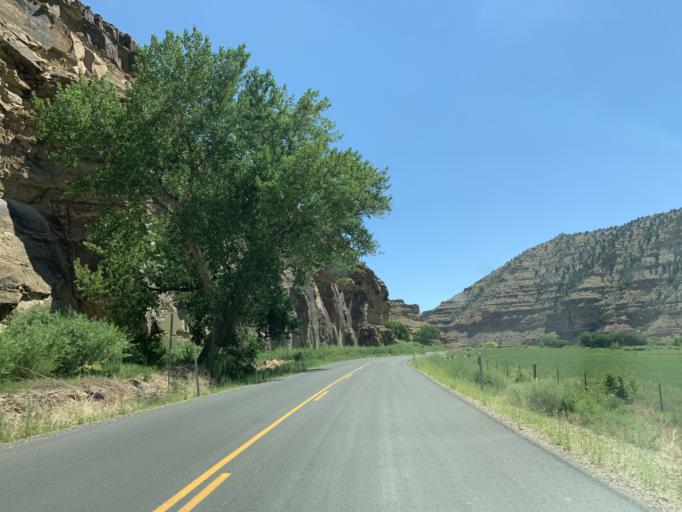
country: US
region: Utah
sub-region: Carbon County
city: East Carbon City
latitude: 39.8090
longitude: -110.2663
